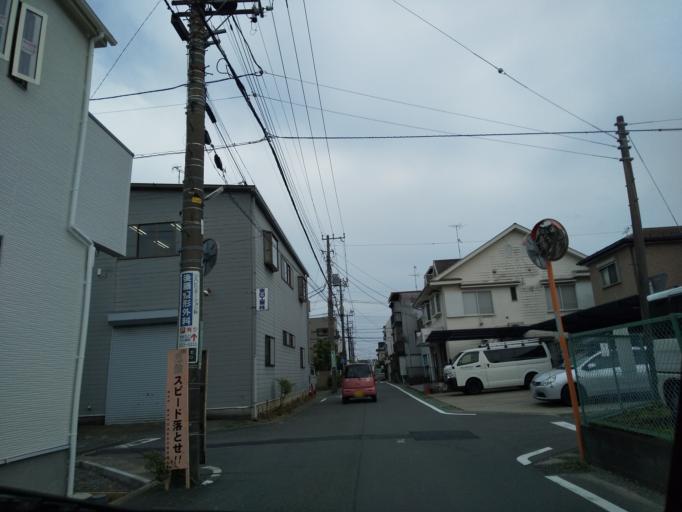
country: JP
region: Kanagawa
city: Atsugi
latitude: 35.4688
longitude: 139.3555
